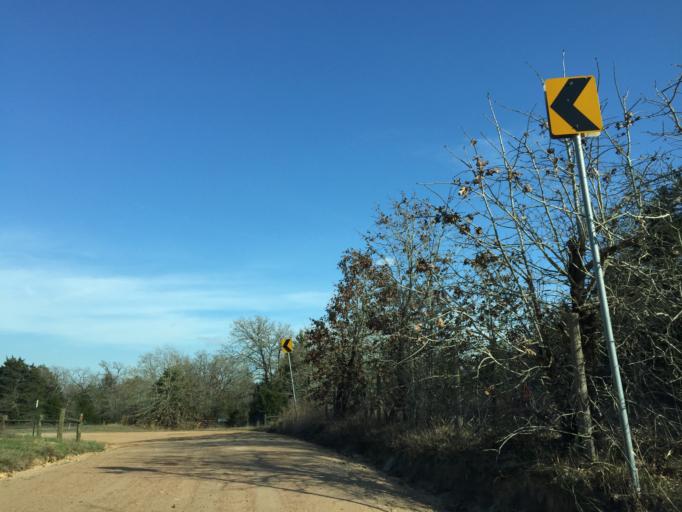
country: US
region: Texas
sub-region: Lee County
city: Lexington
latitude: 30.4449
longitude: -97.1717
